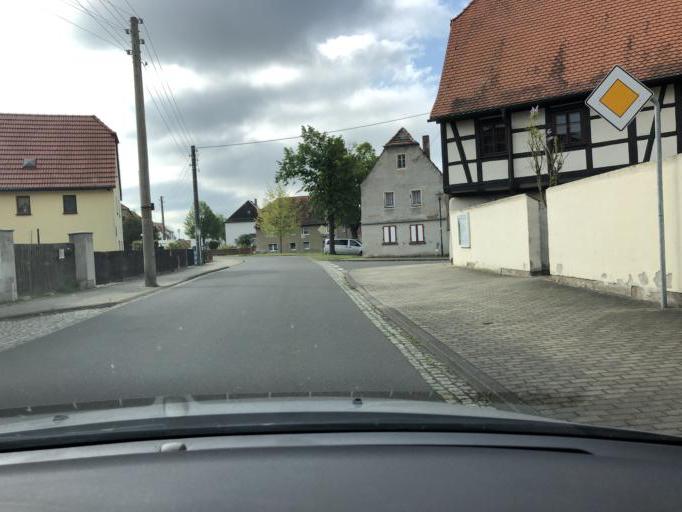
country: DE
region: Saxony
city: Lobstadt
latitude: 51.1320
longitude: 12.4501
